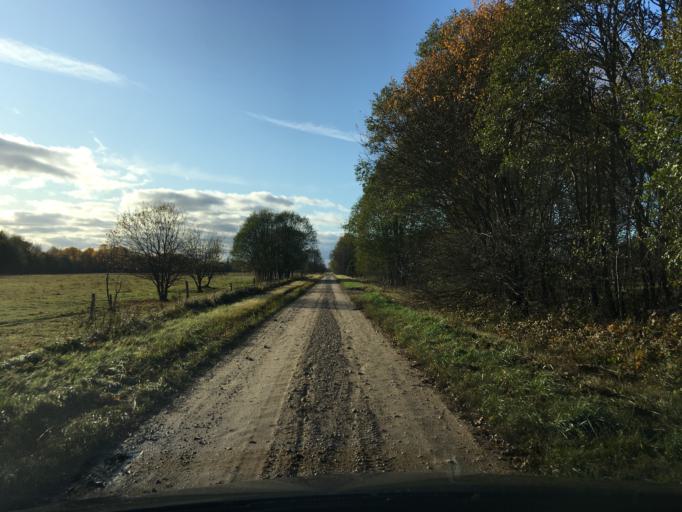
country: EE
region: Laeaene
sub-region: Lihula vald
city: Lihula
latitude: 58.5635
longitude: 23.8154
